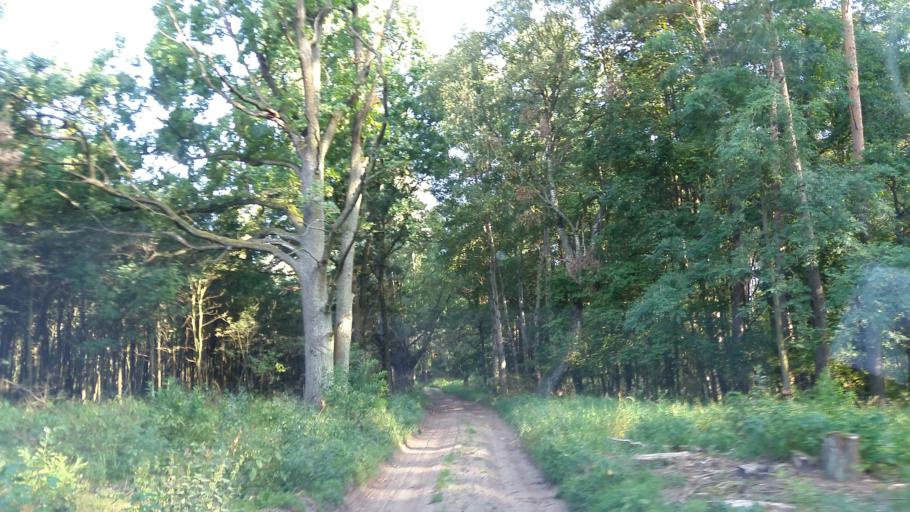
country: PL
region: West Pomeranian Voivodeship
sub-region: Powiat choszczenski
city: Recz
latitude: 53.1982
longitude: 15.5425
